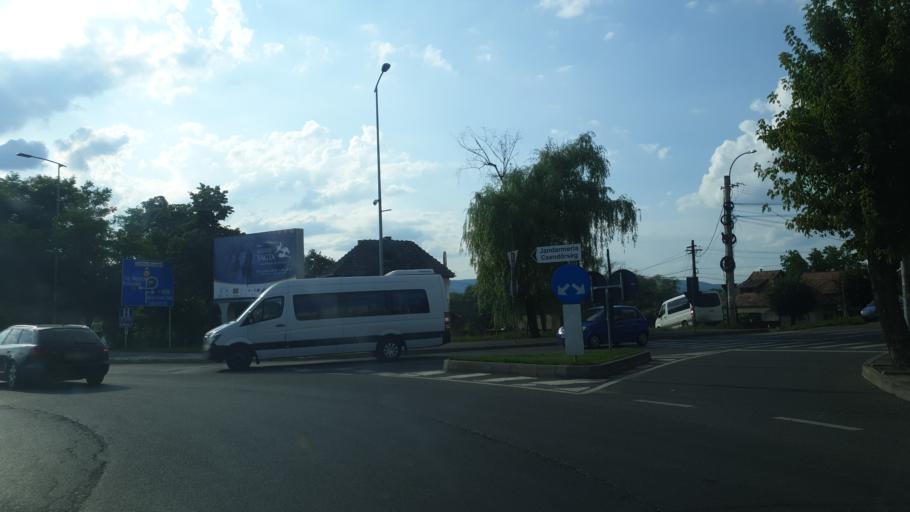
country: RO
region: Covasna
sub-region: Municipiul Sfantu Gheorghe
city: Sfantu-Gheorghe
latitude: 45.8633
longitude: 25.8067
